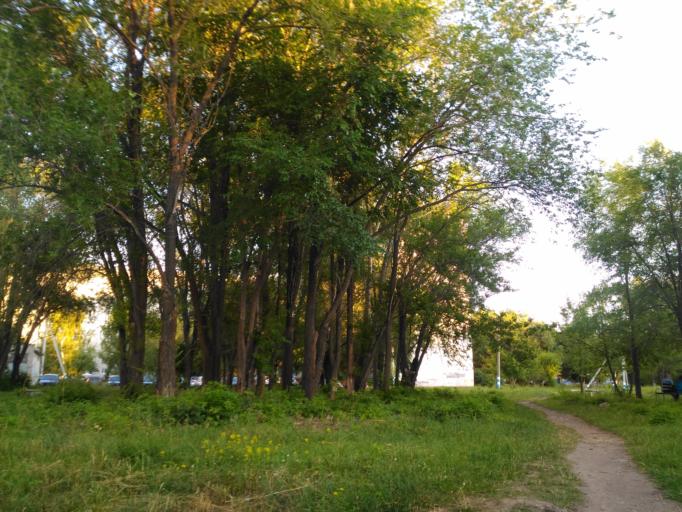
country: RU
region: Ulyanovsk
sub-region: Ulyanovskiy Rayon
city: Ulyanovsk
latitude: 54.3252
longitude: 48.4831
